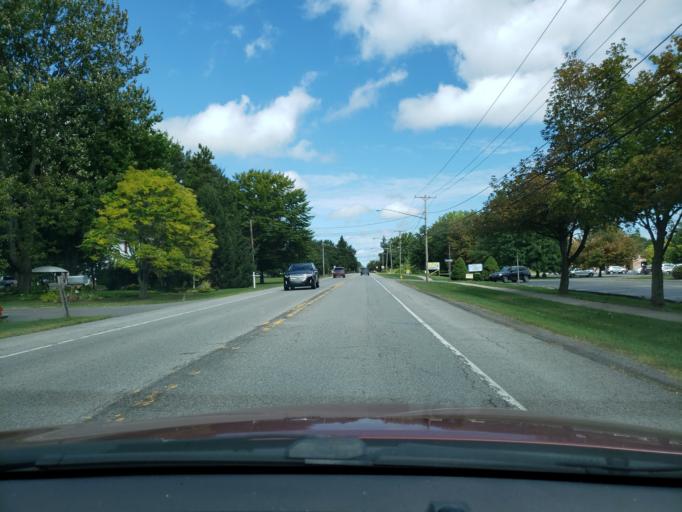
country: US
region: New York
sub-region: Monroe County
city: Greece
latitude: 43.2266
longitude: -77.7337
